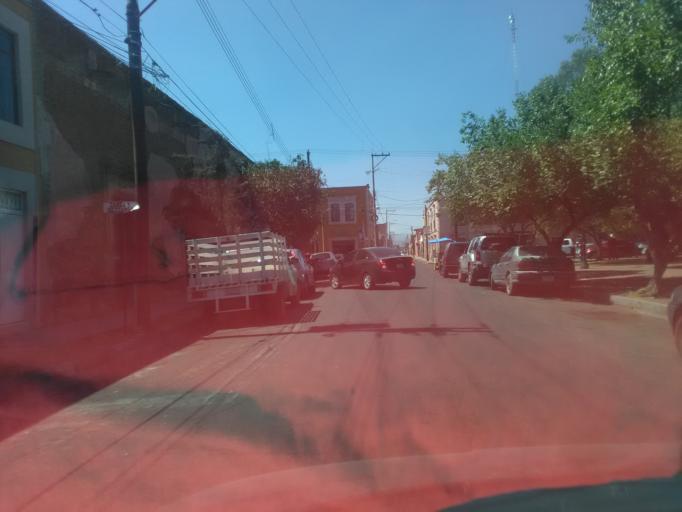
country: MX
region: Durango
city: Victoria de Durango
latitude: 24.0243
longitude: -104.6607
